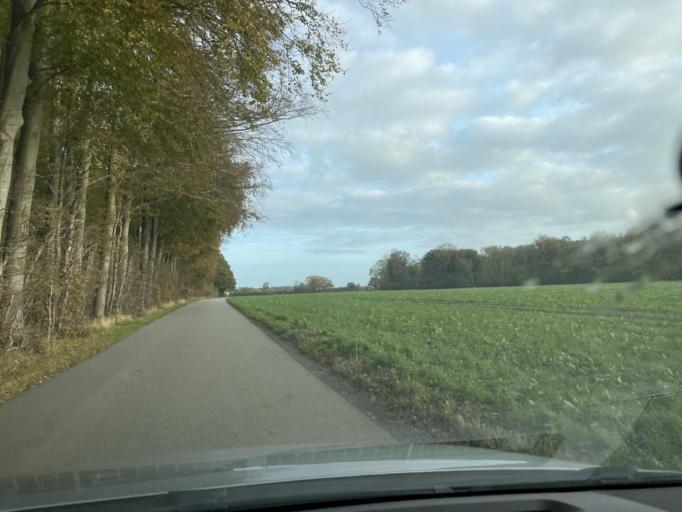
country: DK
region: South Denmark
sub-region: Kerteminde Kommune
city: Kerteminde
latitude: 55.4210
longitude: 10.6748
